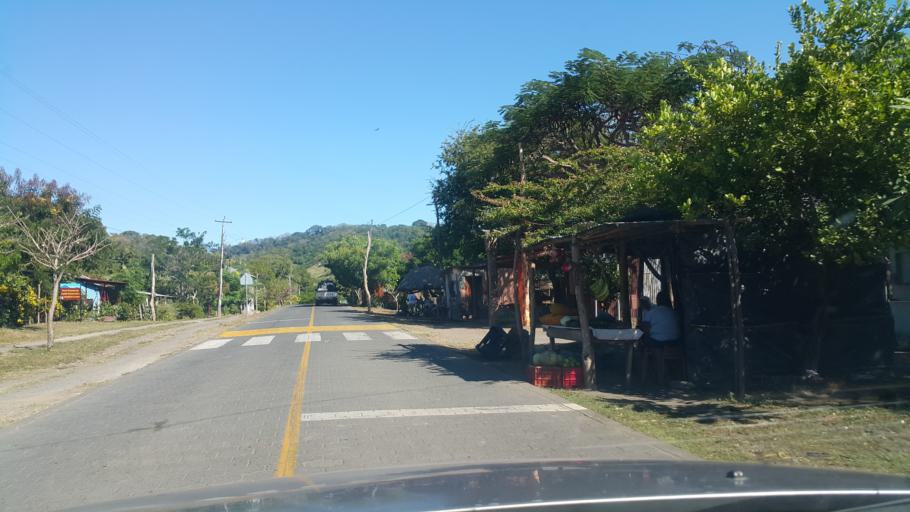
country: NI
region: Rivas
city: Moyogalpa
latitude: 11.4858
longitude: -85.6420
